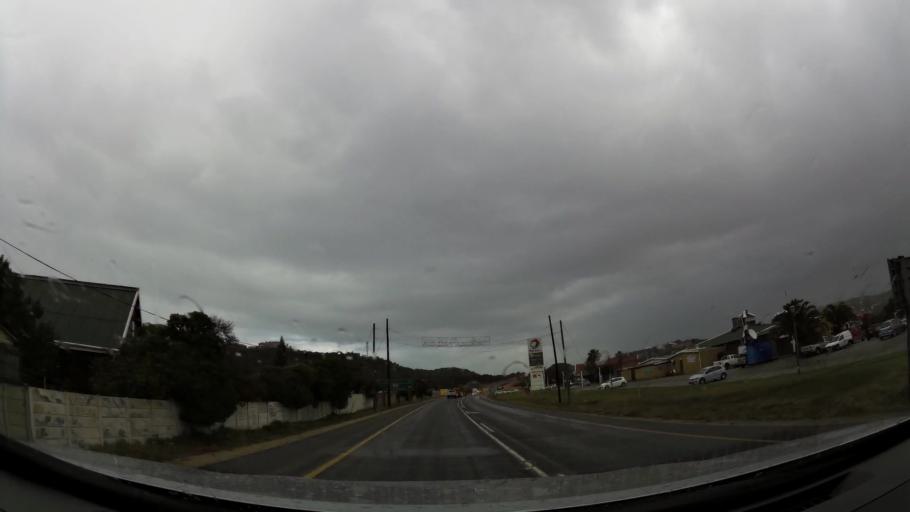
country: ZA
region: Western Cape
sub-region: Eden District Municipality
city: Mossel Bay
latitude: -34.0545
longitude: 22.2258
